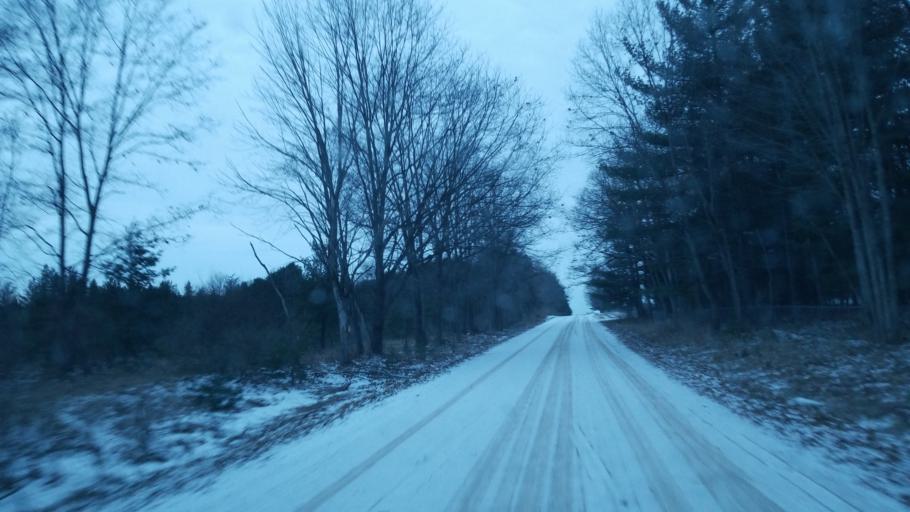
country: US
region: Michigan
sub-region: Osceola County
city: Reed City
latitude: 43.8436
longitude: -85.4164
